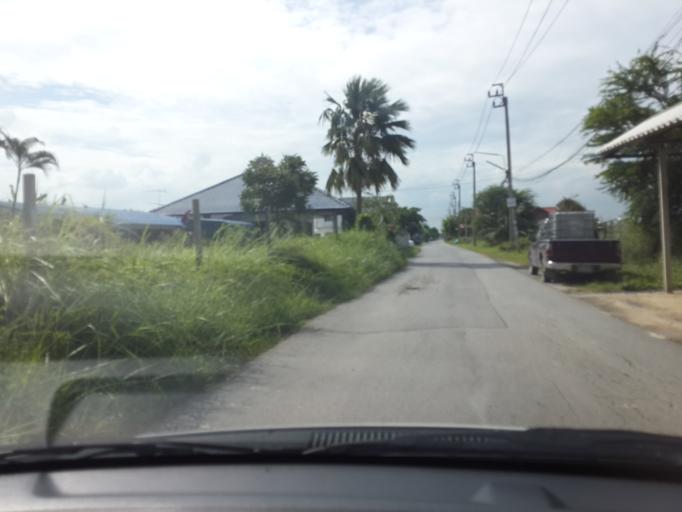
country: TH
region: Bangkok
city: Khlong Sam Wa
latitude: 13.8439
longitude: 100.7852
